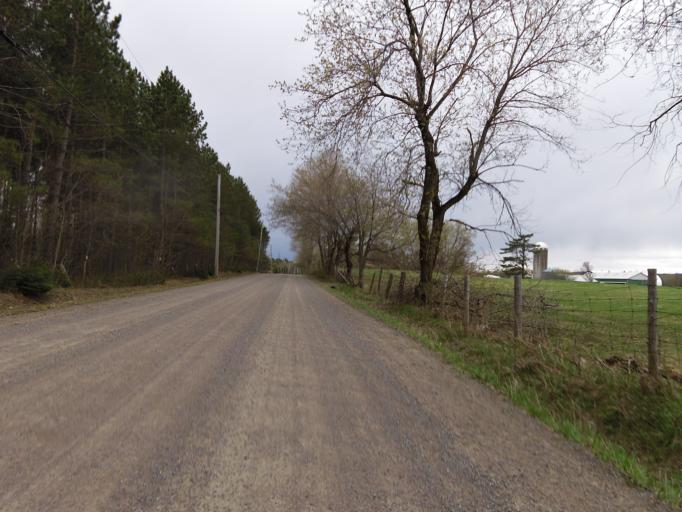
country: CA
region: Ontario
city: Hawkesbury
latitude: 45.6187
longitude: -74.5365
